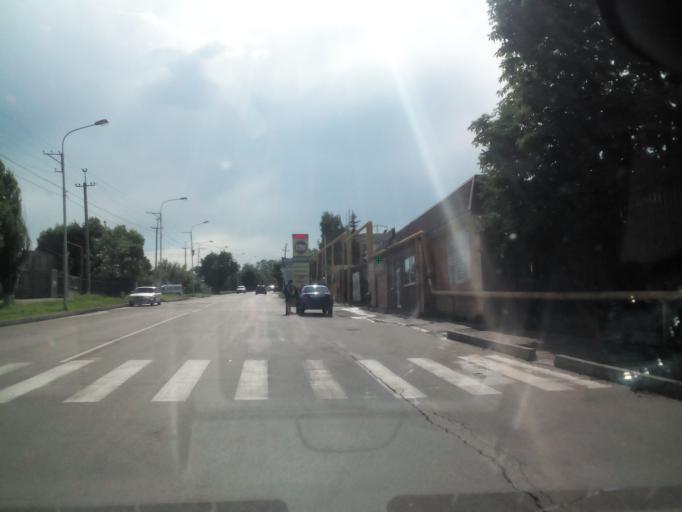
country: RU
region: Stavropol'skiy
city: Stavropol'
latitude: 45.0327
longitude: 42.0067
